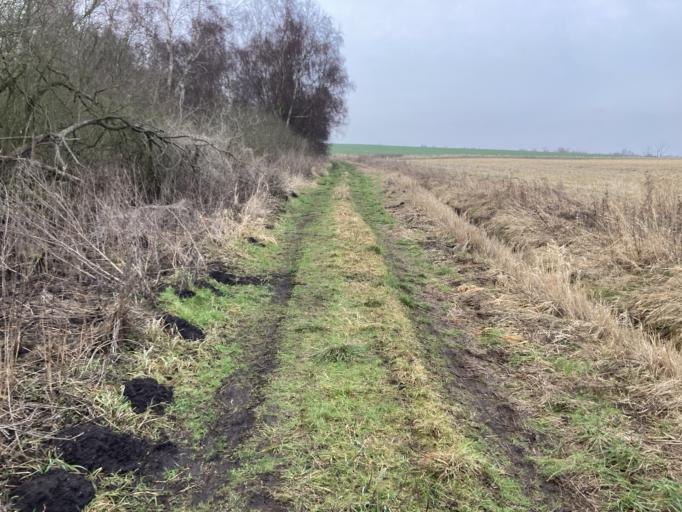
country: DK
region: Capital Region
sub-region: Hoje-Taastrup Kommune
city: Taastrup
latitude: 55.6901
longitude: 12.2782
